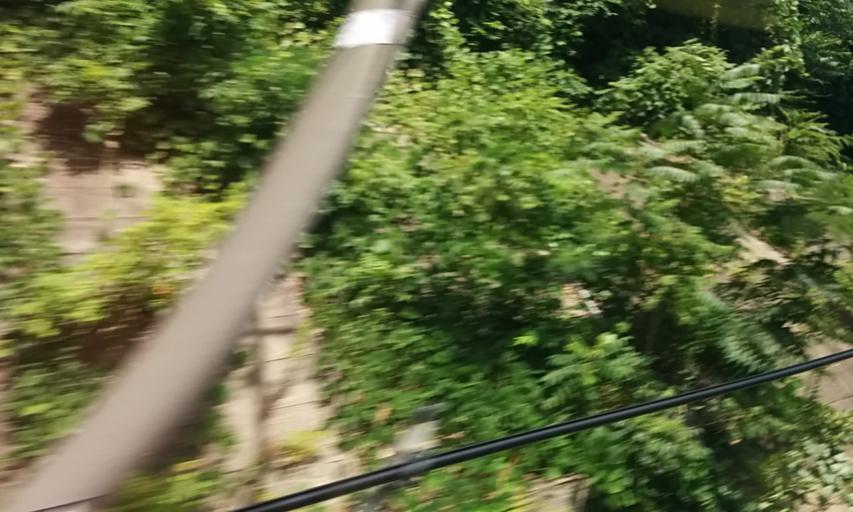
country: JP
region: Fukushima
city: Motomiya
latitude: 37.5251
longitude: 140.4369
